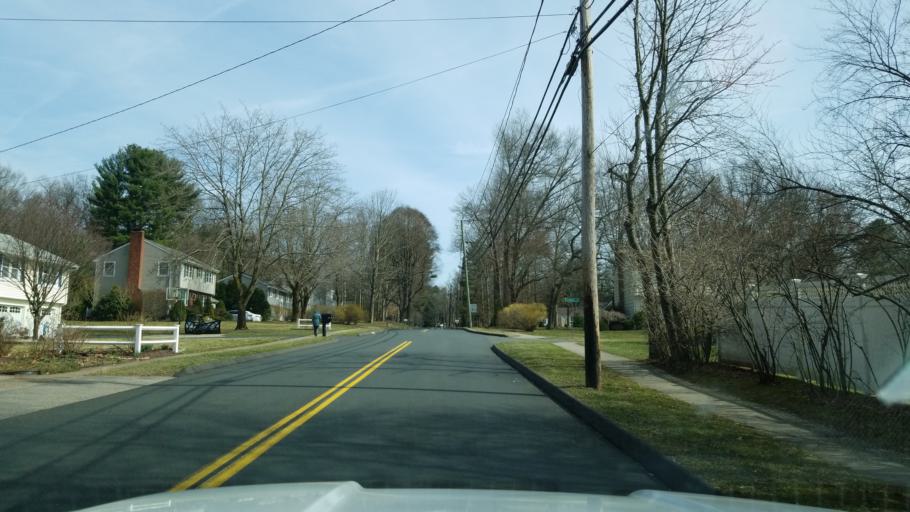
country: US
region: Connecticut
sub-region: Hartford County
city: Glastonbury Center
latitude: 41.7042
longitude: -72.5785
